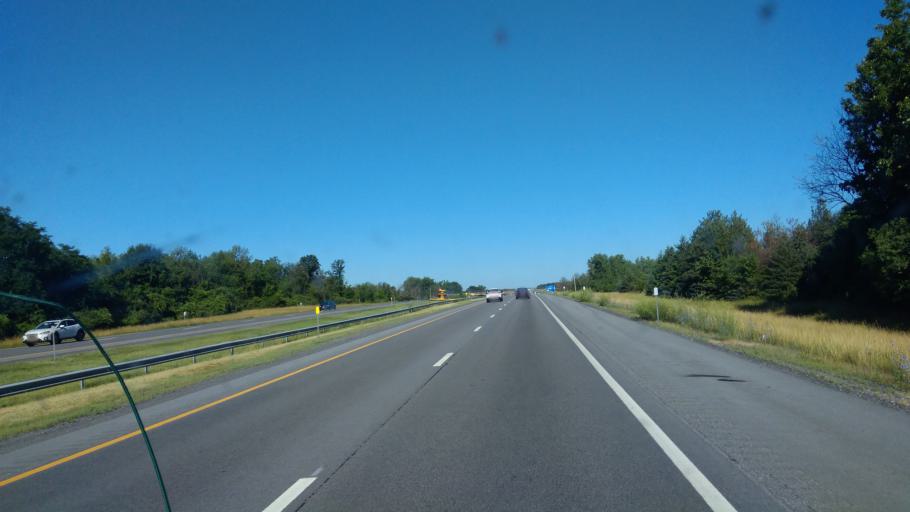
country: US
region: New York
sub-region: Livingston County
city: Caledonia
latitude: 43.0301
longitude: -77.8694
